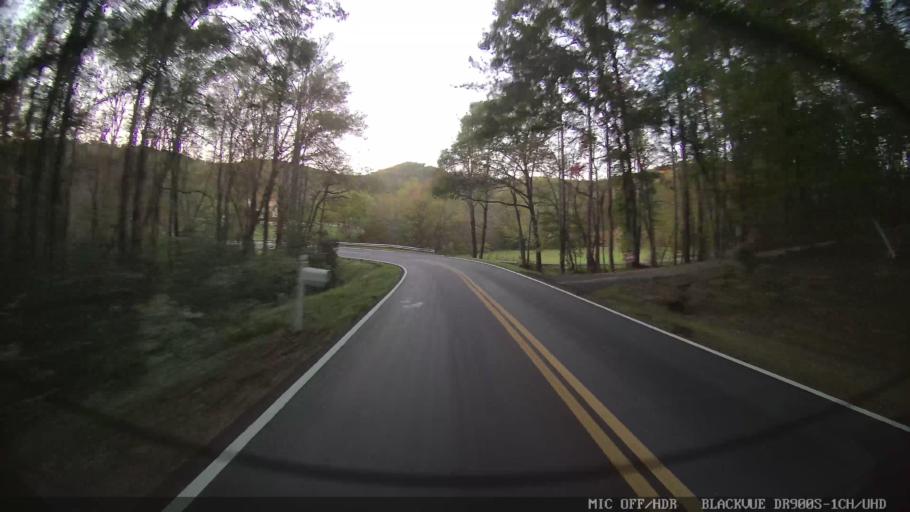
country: US
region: Georgia
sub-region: Union County
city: Blairsville
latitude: 34.8557
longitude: -83.9028
